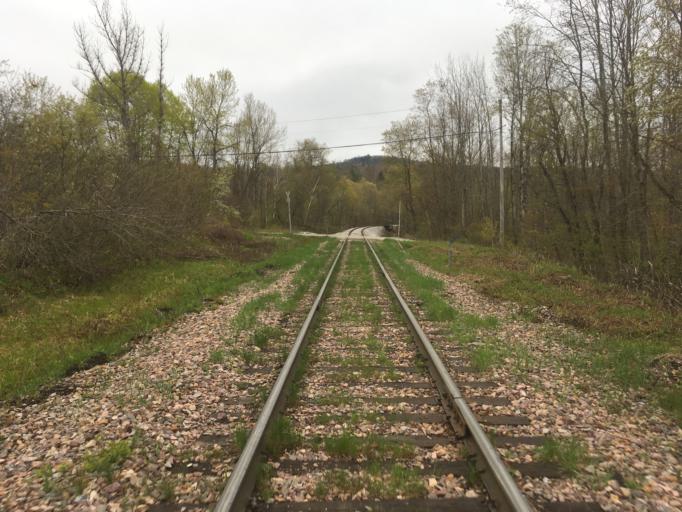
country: US
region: Vermont
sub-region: Rutland County
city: Rutland
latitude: 43.4772
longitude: -72.8734
